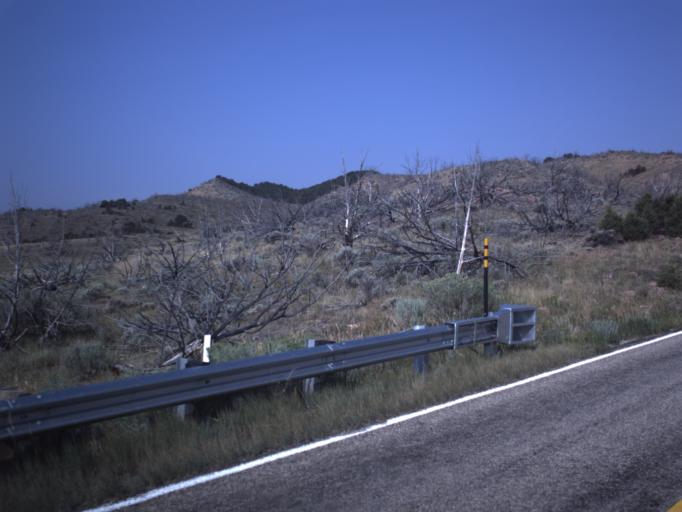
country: US
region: Utah
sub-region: Daggett County
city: Manila
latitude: 40.9468
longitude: -109.4395
